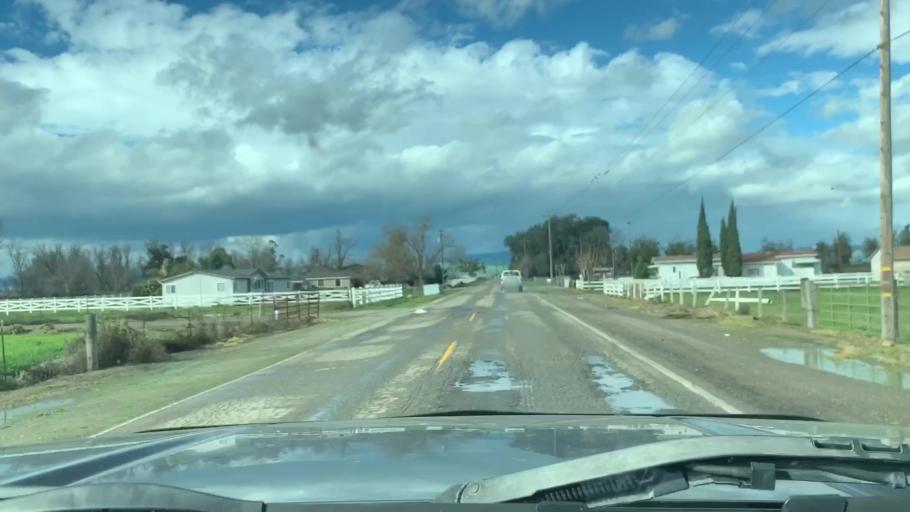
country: US
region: California
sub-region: Merced County
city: Gustine
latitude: 37.1221
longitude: -120.9728
